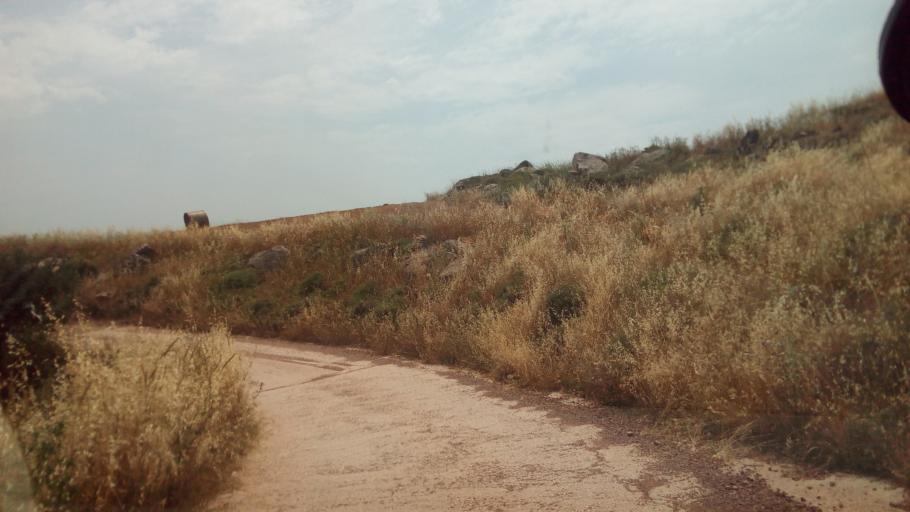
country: CY
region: Pafos
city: Polis
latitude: 34.9818
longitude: 32.3547
